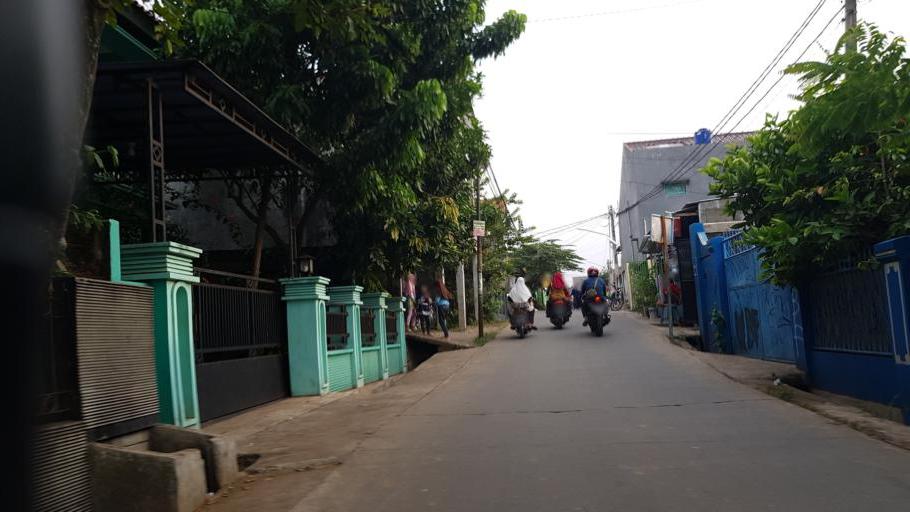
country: ID
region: West Java
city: Depok
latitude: -6.3911
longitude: 106.7979
